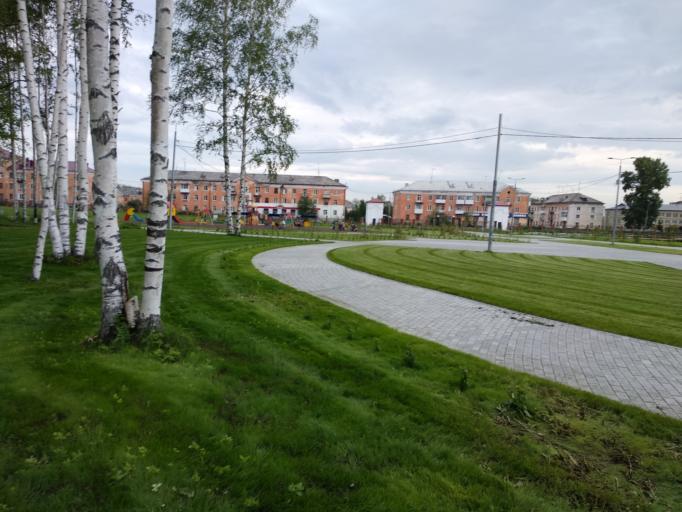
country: RU
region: Sverdlovsk
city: Volchansk
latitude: 59.9055
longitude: 60.0164
